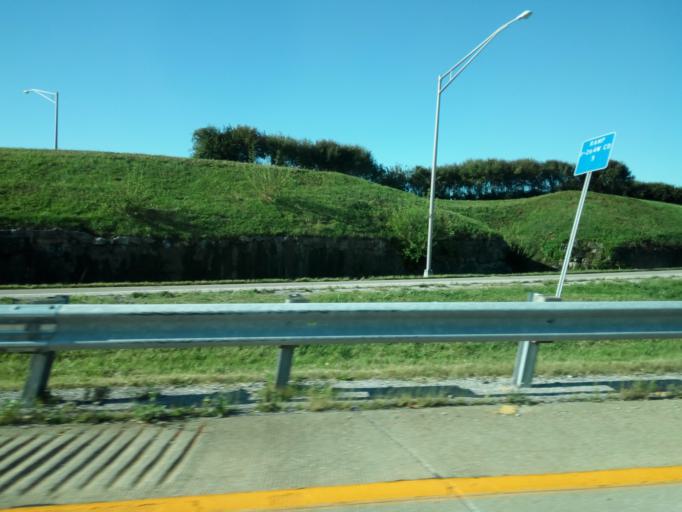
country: US
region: Kentucky
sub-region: Jefferson County
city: Audubon Park
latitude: 38.1909
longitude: -85.7338
